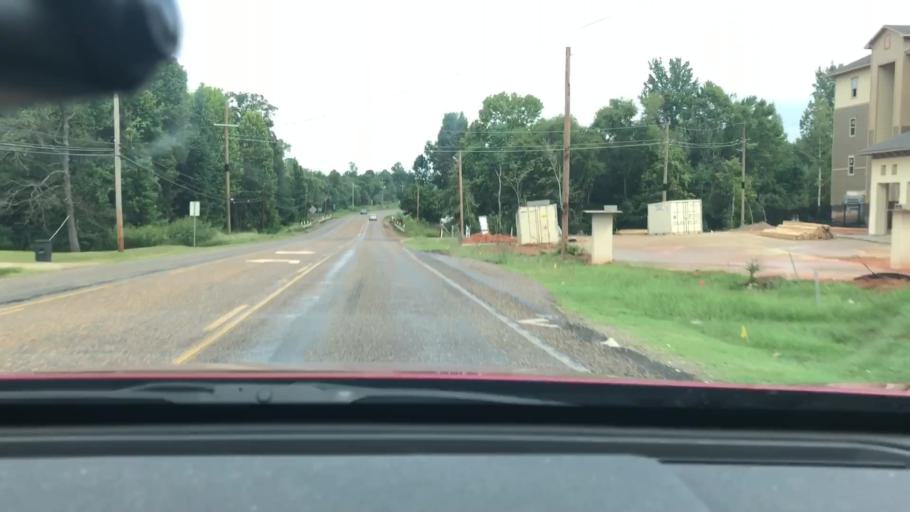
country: US
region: Texas
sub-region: Bowie County
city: Wake Village
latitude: 33.4432
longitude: -94.1097
